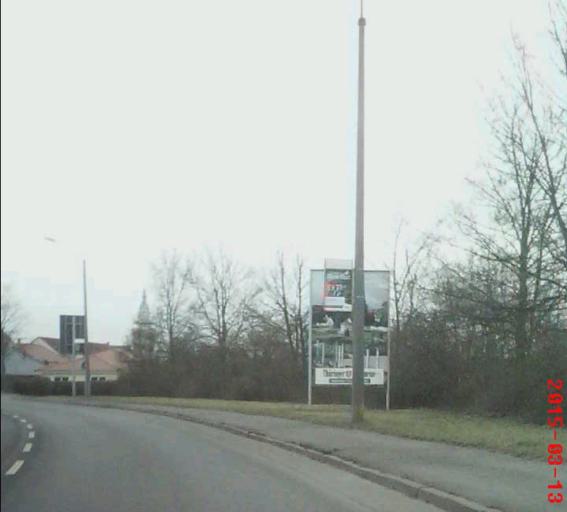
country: DE
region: Thuringia
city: Bad Langensalza
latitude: 51.1125
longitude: 10.6558
